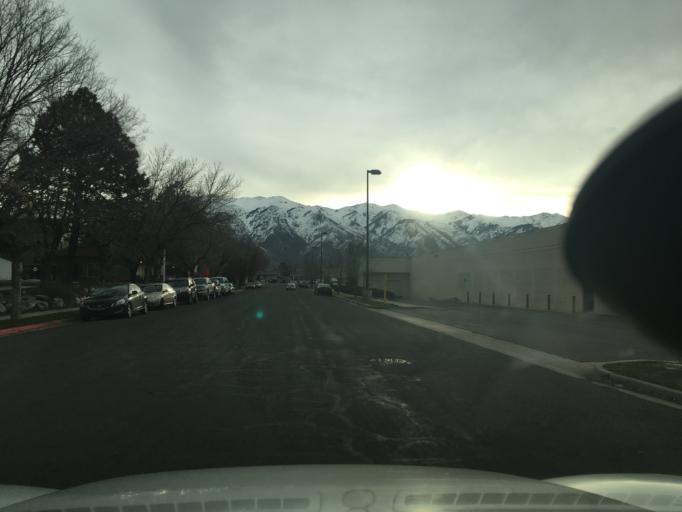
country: US
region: Utah
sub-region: Davis County
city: Layton
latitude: 41.0807
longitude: -111.9768
